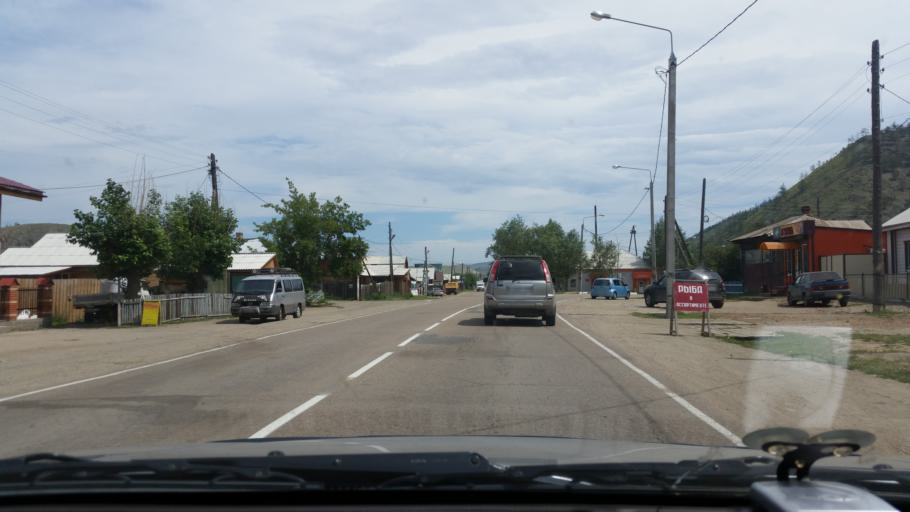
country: RU
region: Irkutsk
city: Yelantsy
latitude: 52.7968
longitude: 106.4055
